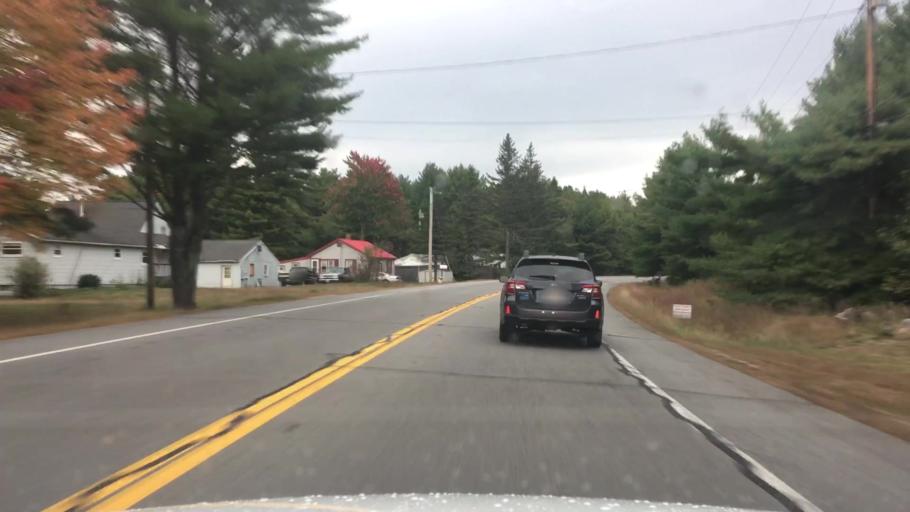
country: US
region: Maine
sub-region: York County
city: Waterboro
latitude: 43.5255
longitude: -70.7195
